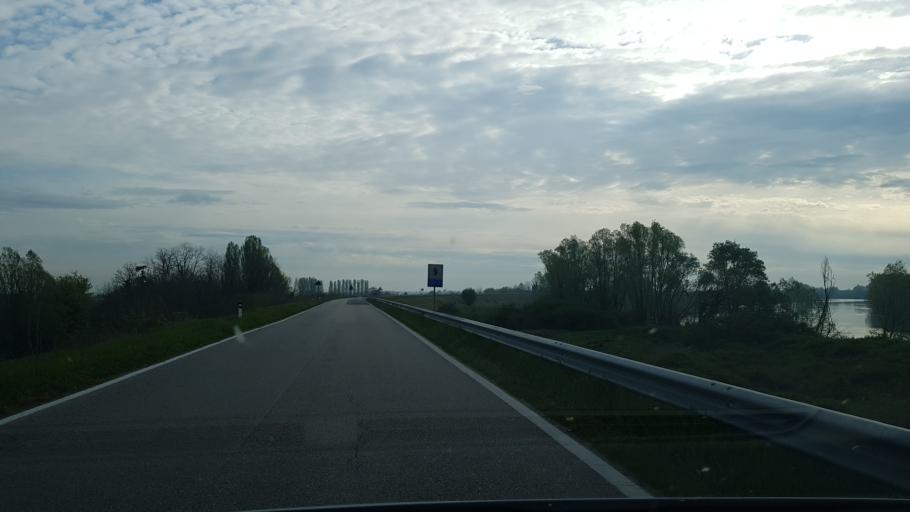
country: IT
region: Veneto
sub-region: Provincia di Padova
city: Barbona
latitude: 45.0985
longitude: 11.7278
